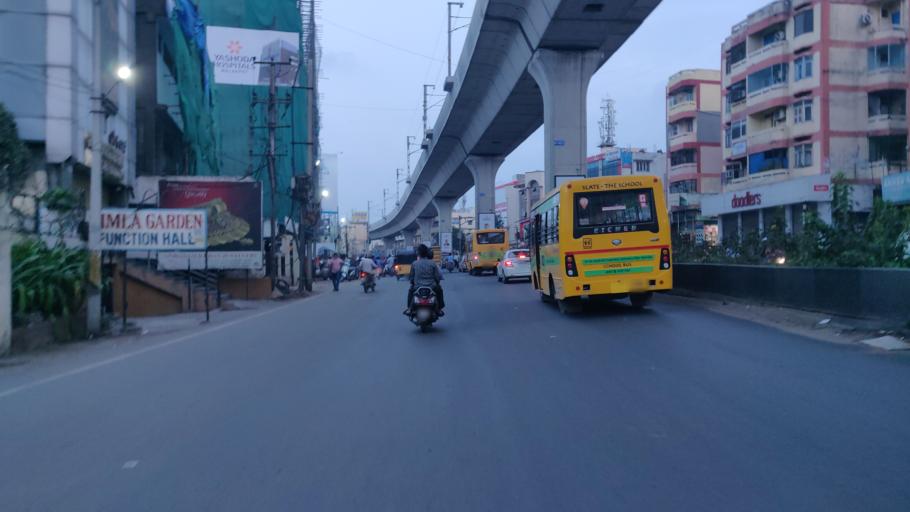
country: IN
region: Telangana
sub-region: Rangareddi
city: Gaddi Annaram
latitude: 17.3747
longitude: 78.4992
